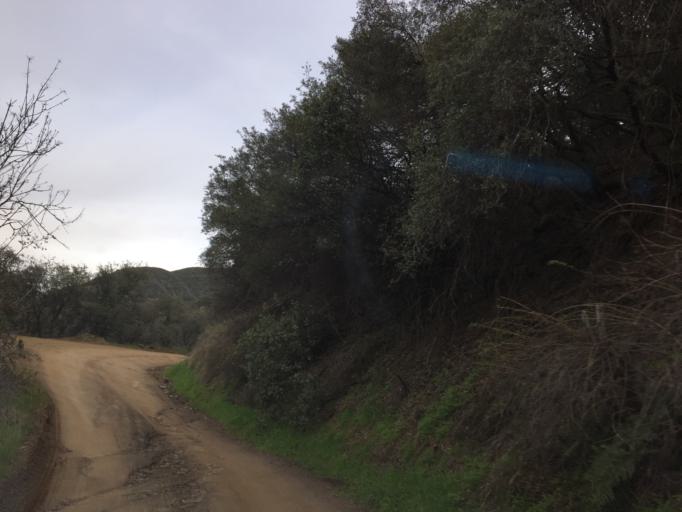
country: US
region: California
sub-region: San Bernardino County
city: Yucaipa
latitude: 34.1144
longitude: -117.0454
